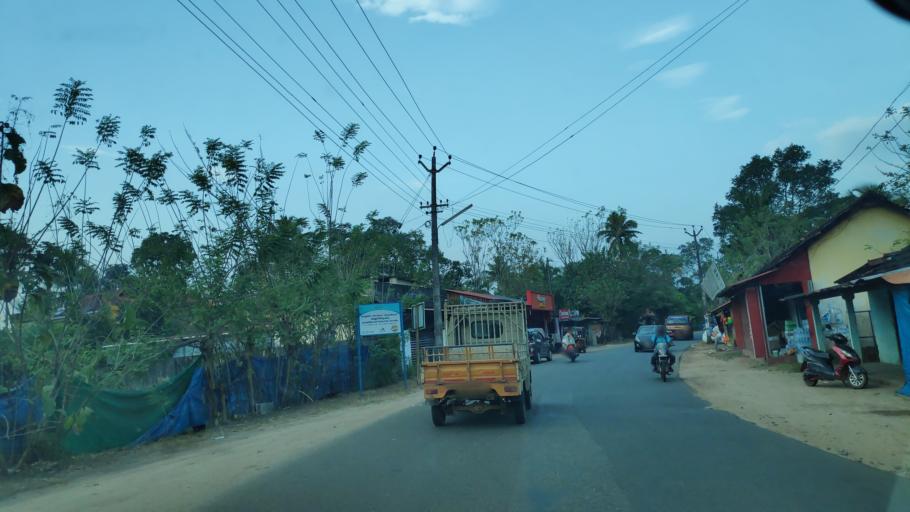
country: IN
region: Kerala
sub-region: Alappuzha
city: Shertallai
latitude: 9.6430
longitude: 76.3700
